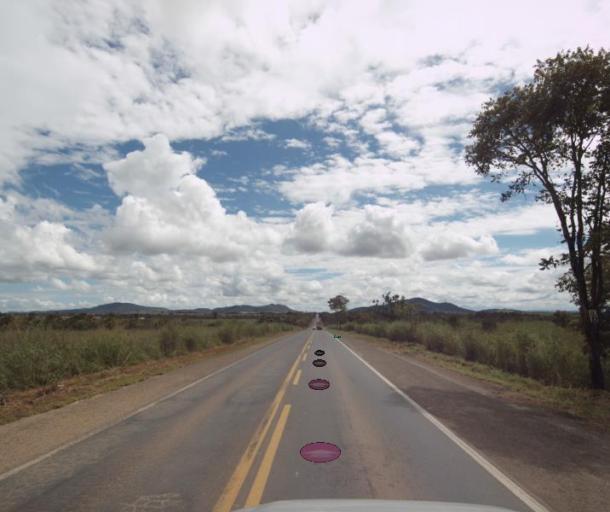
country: BR
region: Goias
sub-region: Uruacu
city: Uruacu
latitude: -14.4560
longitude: -49.1563
